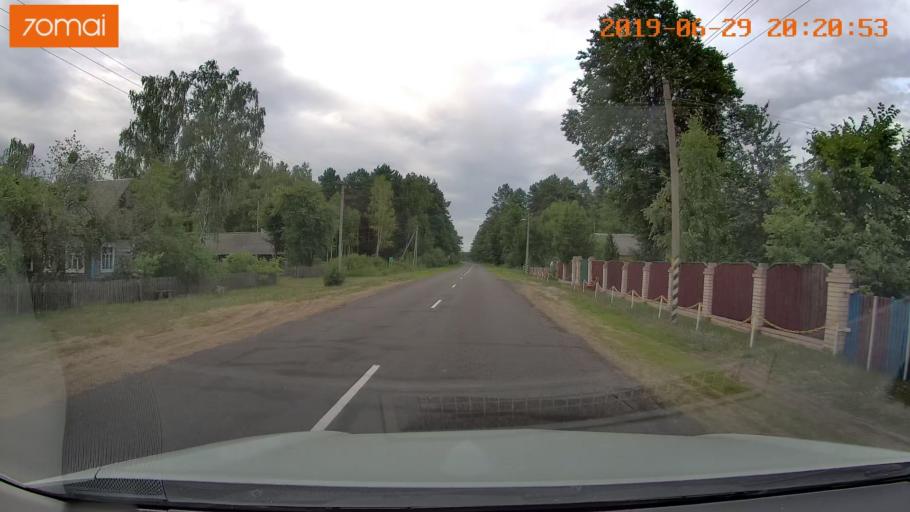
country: BY
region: Brest
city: Asnyezhytsy
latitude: 52.4143
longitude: 26.2510
